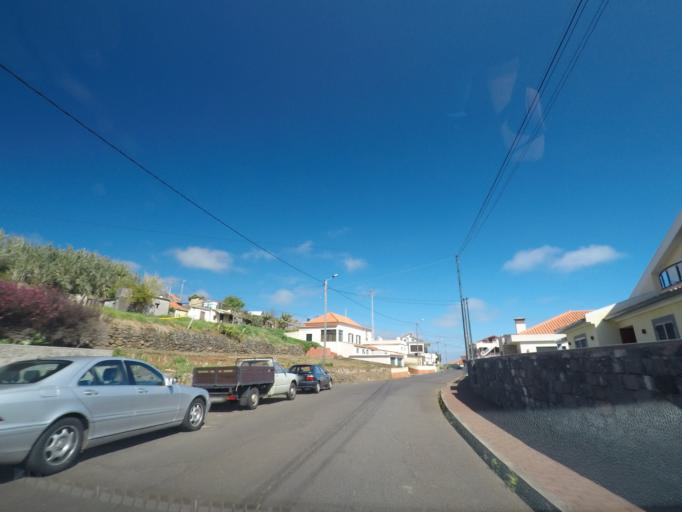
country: PT
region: Madeira
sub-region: Calheta
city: Arco da Calheta
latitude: 32.7011
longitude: -17.1207
